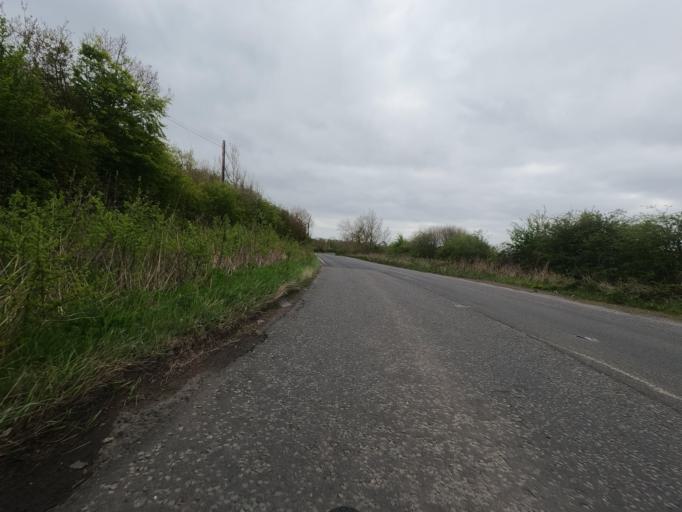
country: GB
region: England
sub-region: Newcastle upon Tyne
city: Dinnington
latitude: 55.0639
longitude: -1.6844
